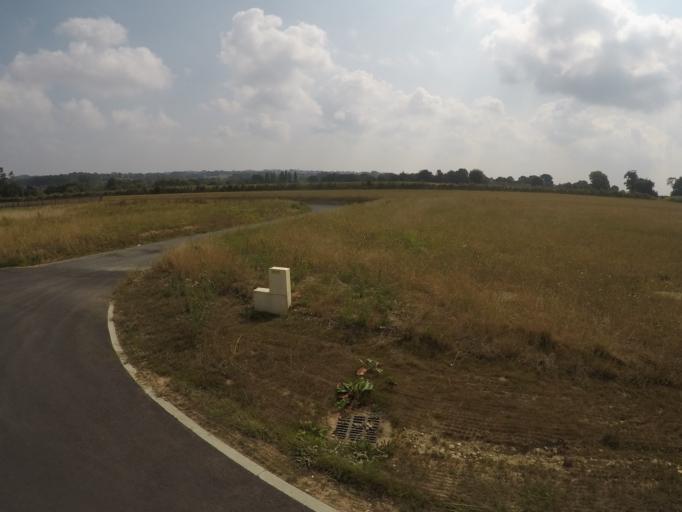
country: FR
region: Brittany
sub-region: Departement des Cotes-d'Armor
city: Plelo
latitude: 48.5300
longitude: -2.9343
